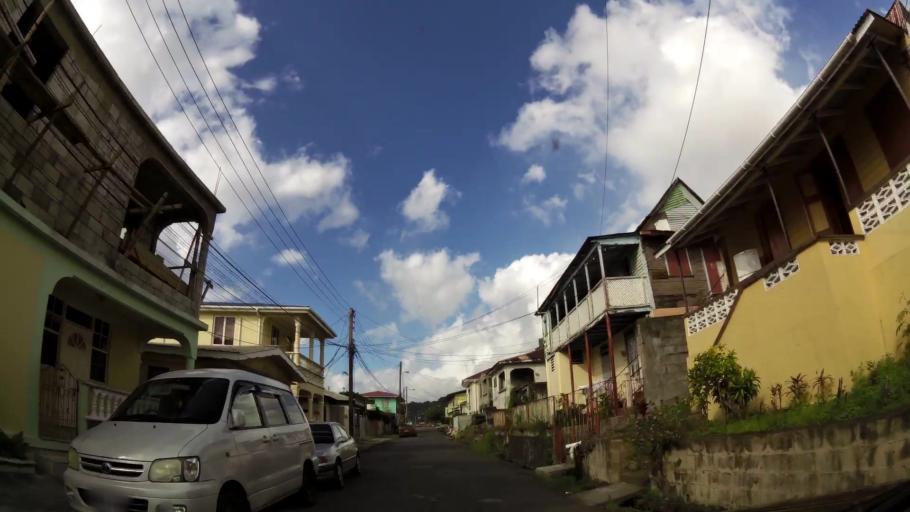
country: DM
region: Saint George
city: Roseau
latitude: 15.3038
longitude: -61.3894
